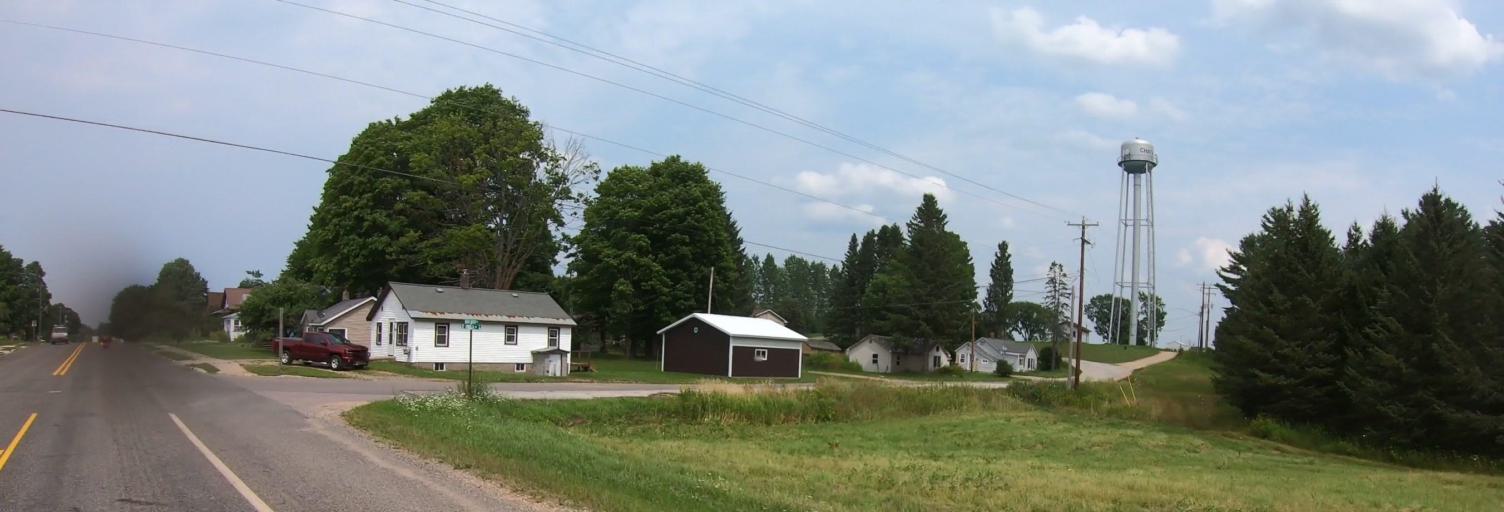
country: US
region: Michigan
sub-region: Alger County
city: Munising
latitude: 46.3438
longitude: -86.9288
